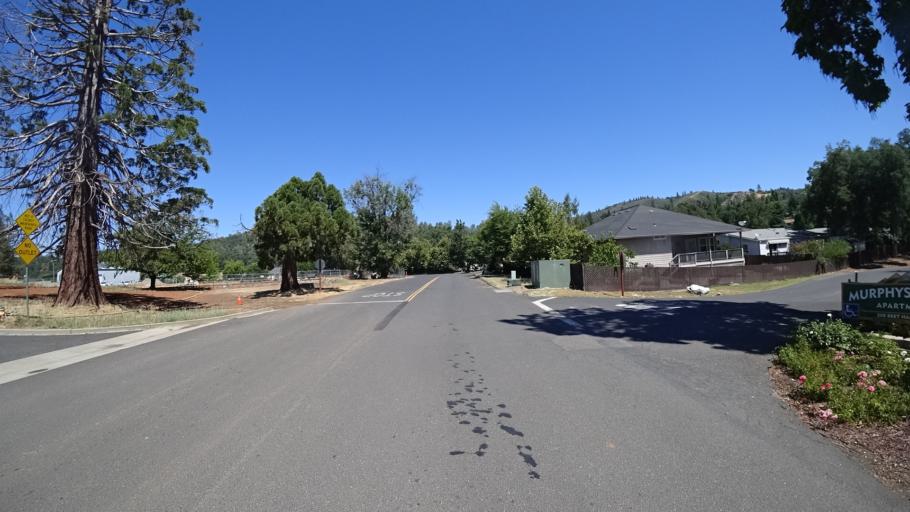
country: US
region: California
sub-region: Calaveras County
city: Murphys
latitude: 38.1421
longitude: -120.4567
